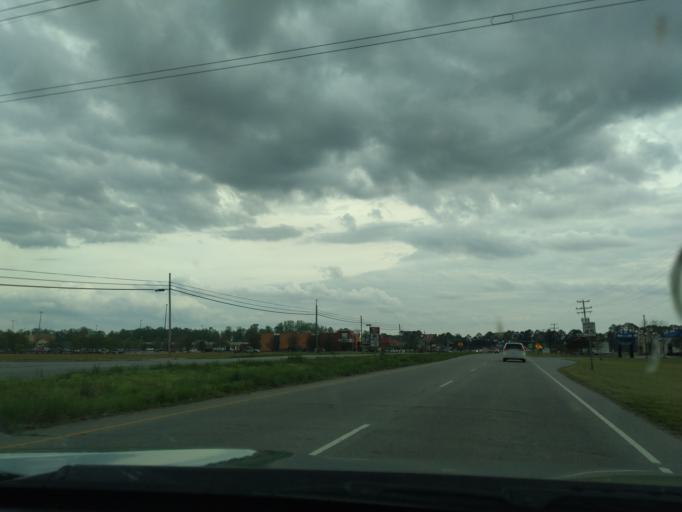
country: US
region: North Carolina
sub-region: Martin County
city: Williamston
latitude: 35.8368
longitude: -77.0657
